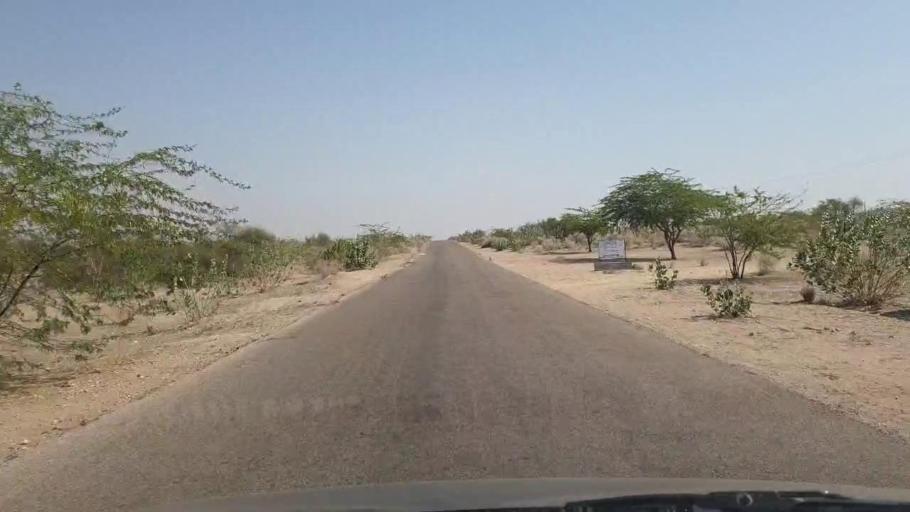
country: PK
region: Sindh
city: Chor
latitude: 25.5493
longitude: 69.8728
